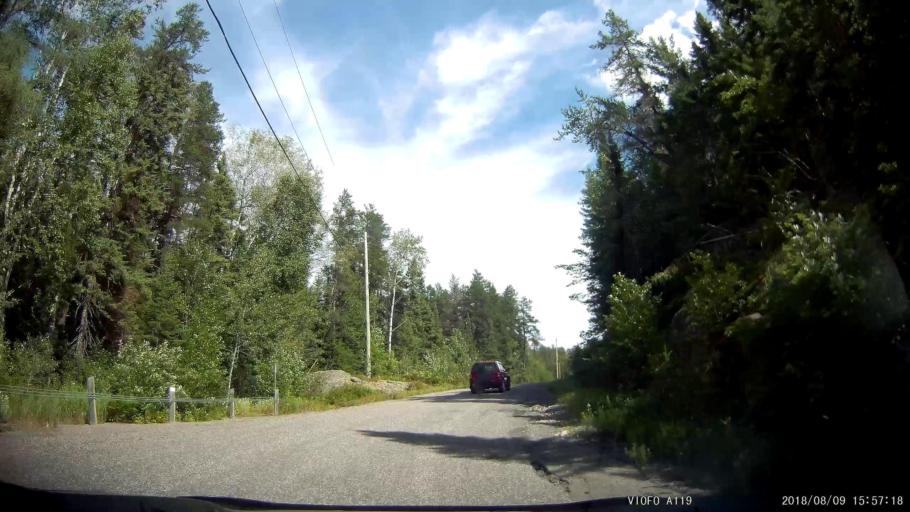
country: CA
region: Ontario
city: Rayside-Balfour
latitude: 46.6075
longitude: -81.5071
